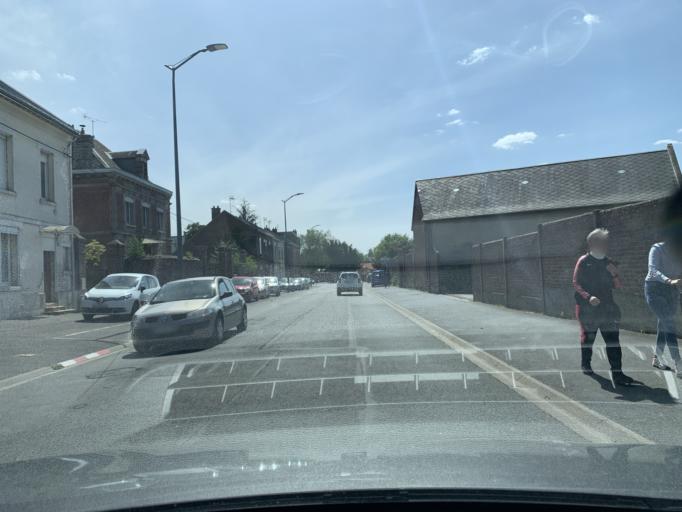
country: FR
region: Picardie
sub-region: Departement de l'Aisne
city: Saint-Quentin
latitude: 49.8613
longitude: 3.2909
